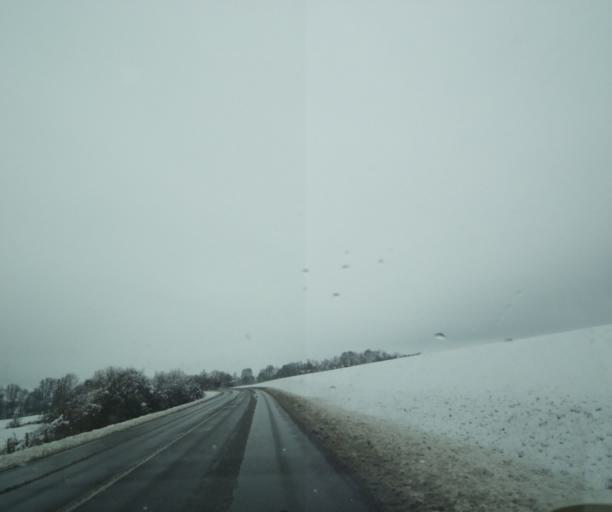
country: FR
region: Champagne-Ardenne
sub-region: Departement de la Haute-Marne
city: Montier-en-Der
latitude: 48.5100
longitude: 4.7997
